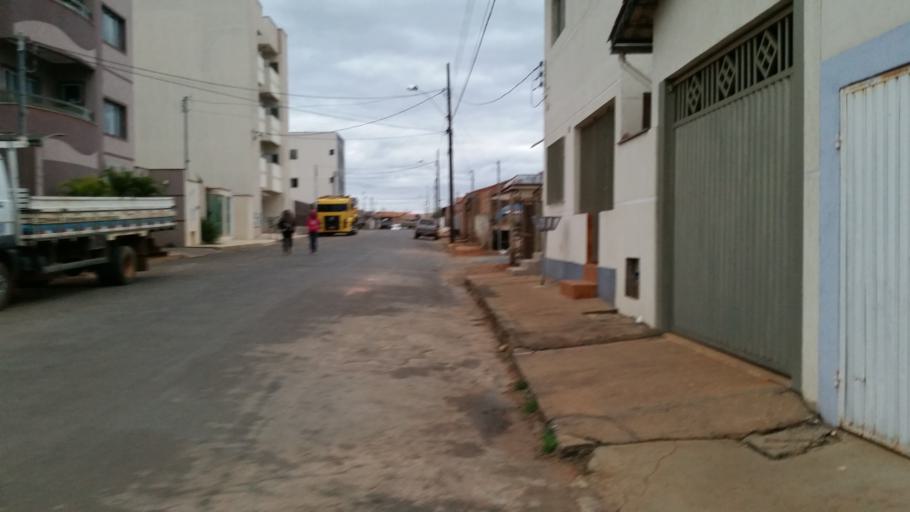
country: BR
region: Minas Gerais
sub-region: Carmo Do Paranaiba
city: Carmo do Paranaiba
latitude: -19.1981
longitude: -46.2377
